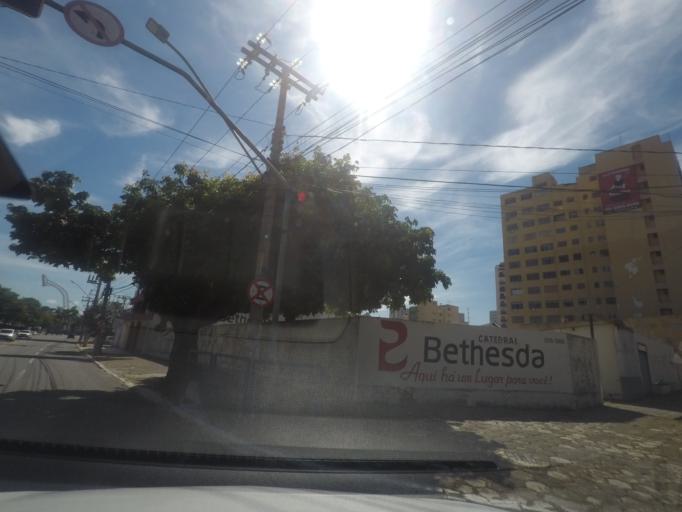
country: BR
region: Goias
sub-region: Goiania
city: Goiania
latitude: -16.6735
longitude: -49.2640
